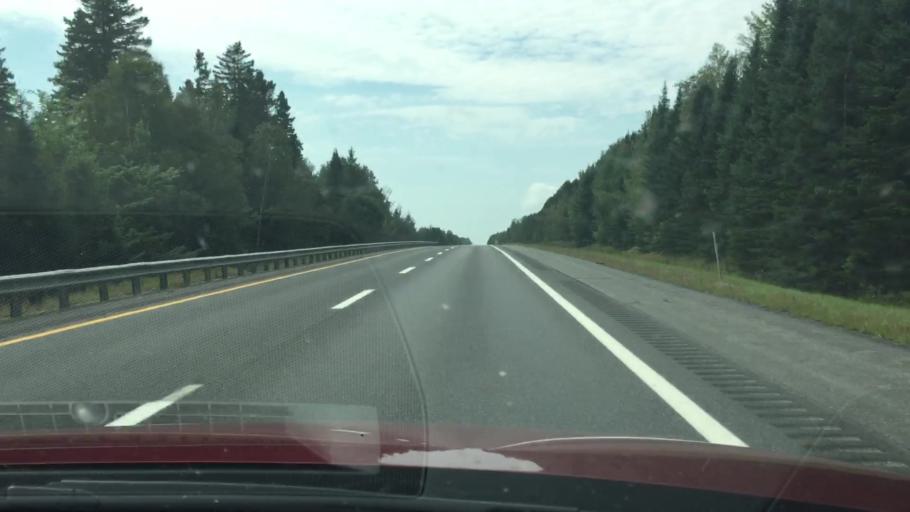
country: US
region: Maine
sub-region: Aroostook County
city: Hodgdon
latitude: 46.1343
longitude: -68.0865
